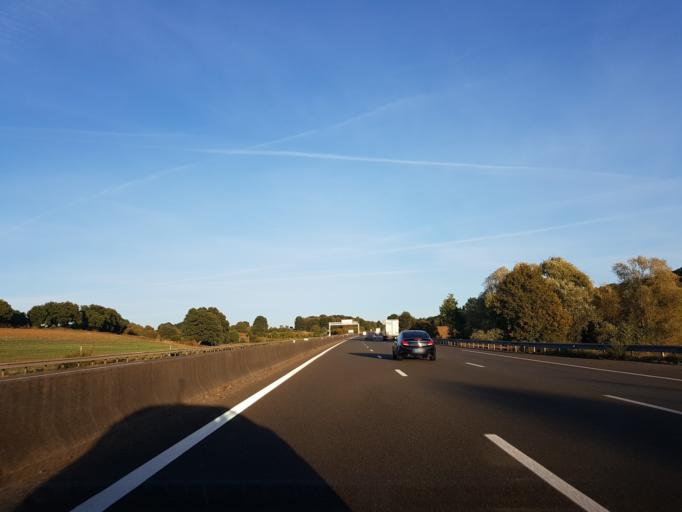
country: FR
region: Pays de la Loire
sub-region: Departement de la Sarthe
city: Sarge-les-le-Mans
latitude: 48.0592
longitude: 0.2263
